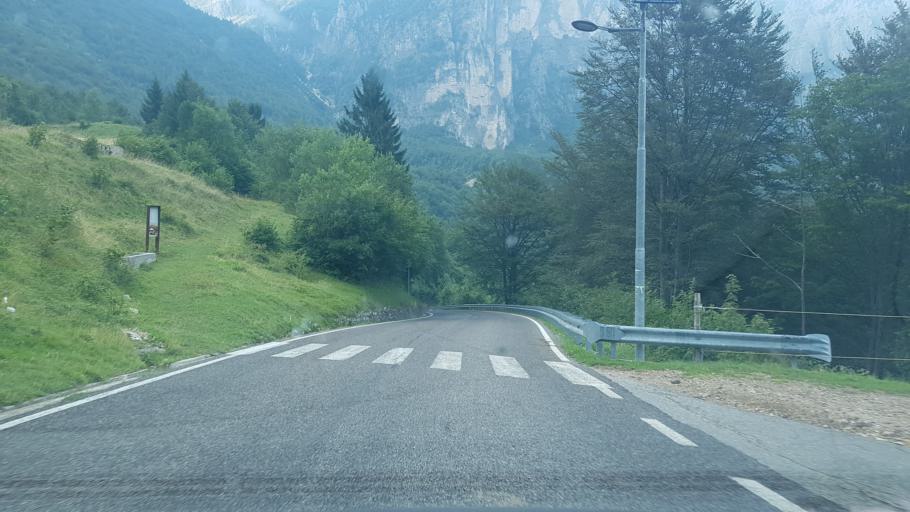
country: IT
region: Veneto
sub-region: Provincia di Vicenza
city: Recoaro Terme
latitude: 45.7593
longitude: 11.1932
